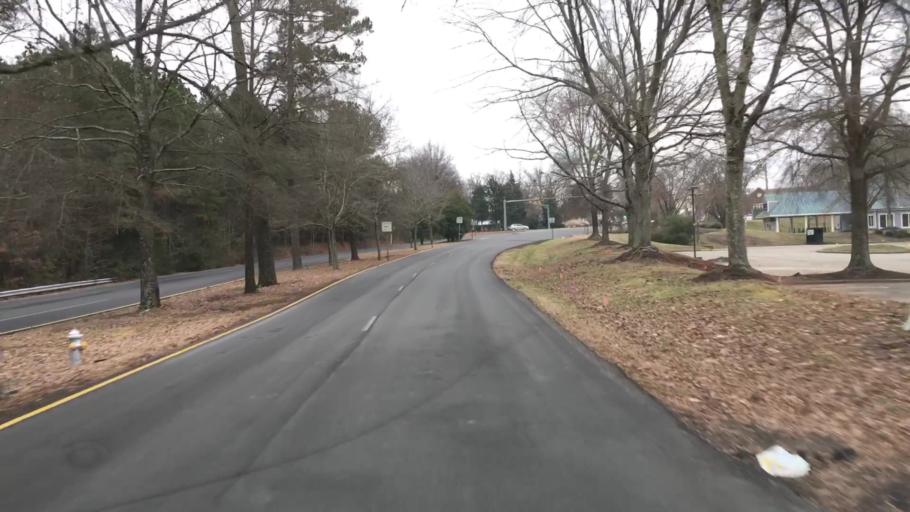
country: US
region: Virginia
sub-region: Chesterfield County
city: Bon Air
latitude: 37.5391
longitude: -77.5634
